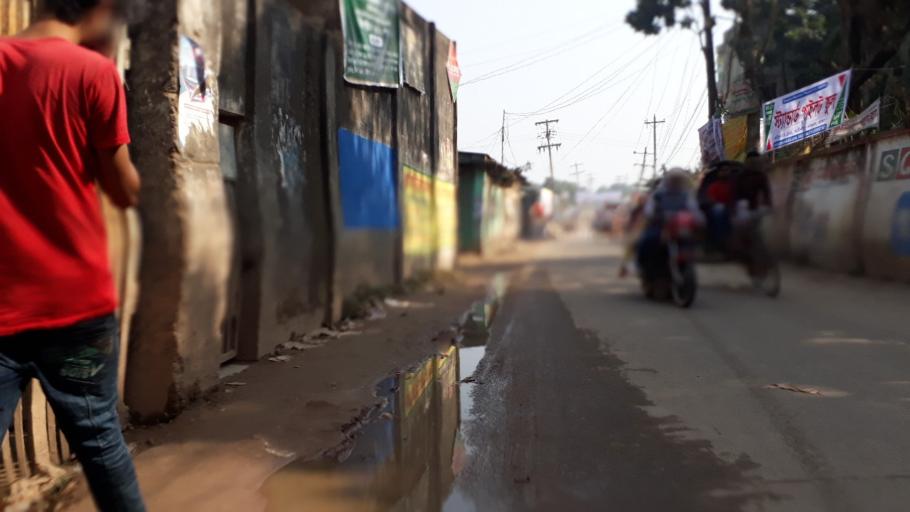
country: BD
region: Dhaka
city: Tungi
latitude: 23.8482
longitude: 90.2664
